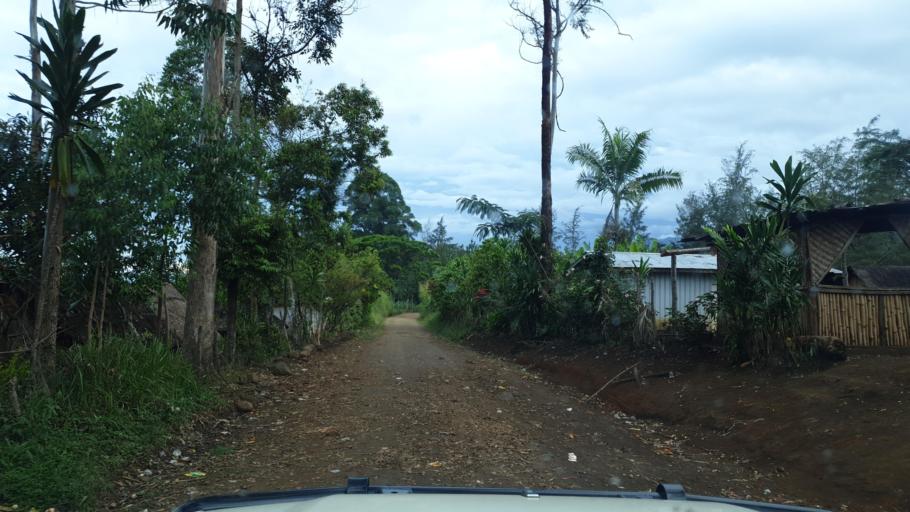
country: PG
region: Eastern Highlands
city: Goroka
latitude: -5.9550
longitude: 145.2726
